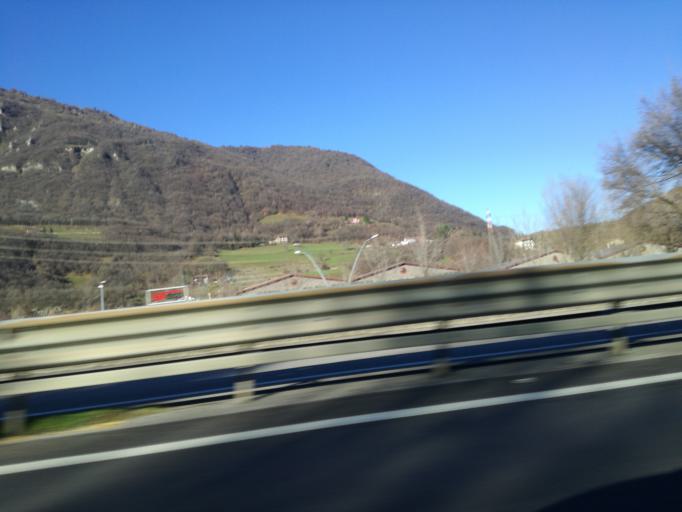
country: IT
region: Lombardy
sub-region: Provincia di Bergamo
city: Sovere
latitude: 45.8057
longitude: 10.0248
